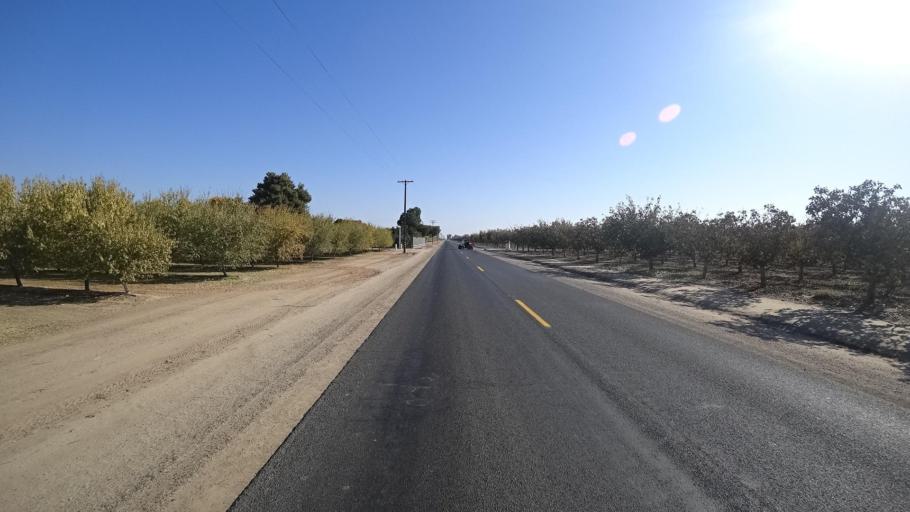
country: US
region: California
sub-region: Kern County
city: Delano
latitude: 35.7177
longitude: -119.3446
